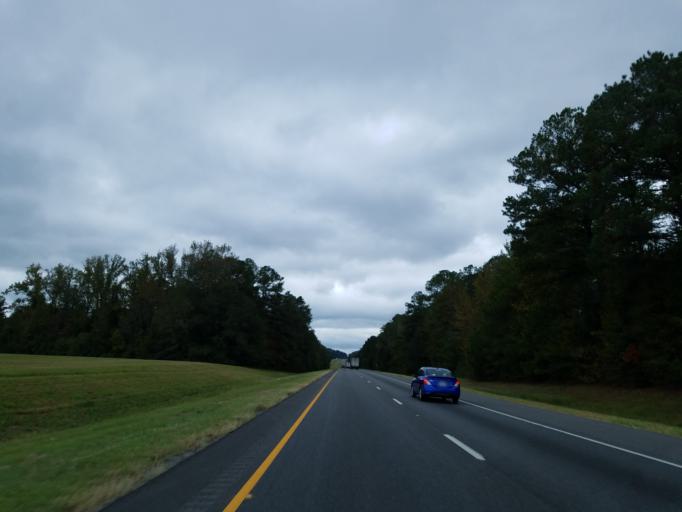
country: US
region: Alabama
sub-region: Hale County
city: Moundville
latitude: 33.0050
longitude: -87.7652
